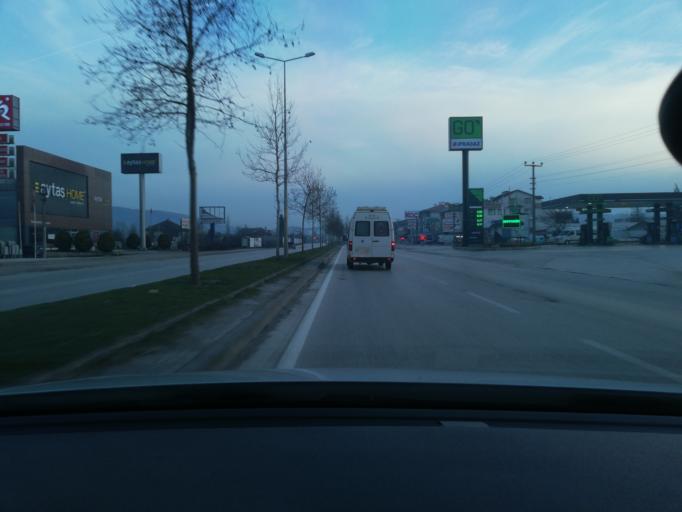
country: TR
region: Duzce
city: Duzce
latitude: 40.8622
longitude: 31.1675
